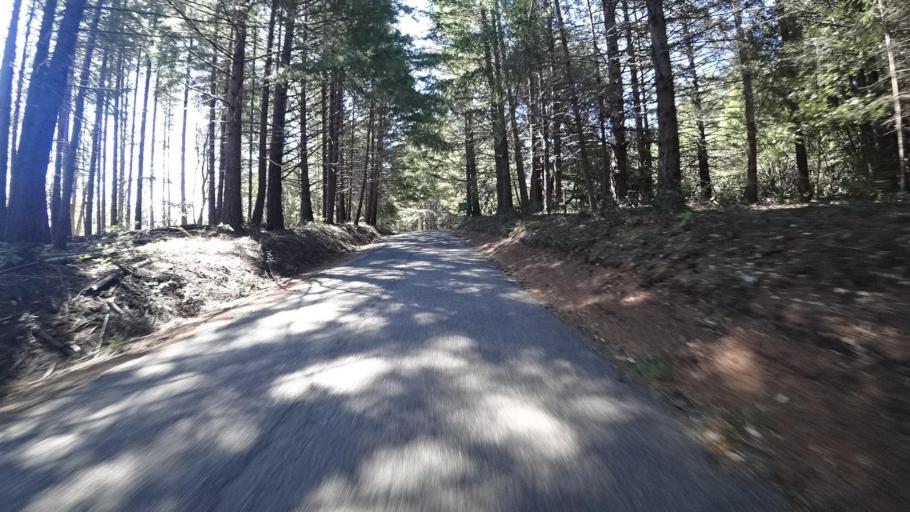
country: US
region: California
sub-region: Humboldt County
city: Redway
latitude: 40.1602
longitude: -124.0801
